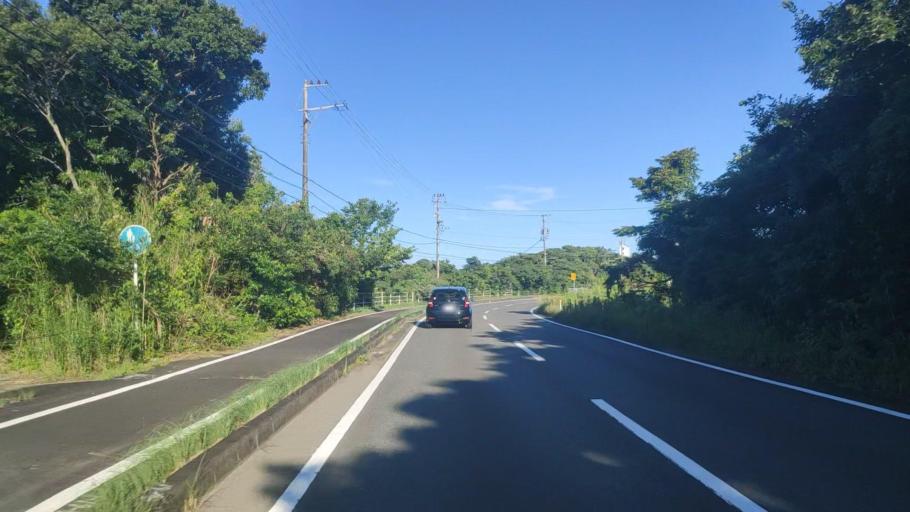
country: JP
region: Mie
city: Toba
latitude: 34.3284
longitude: 136.8733
